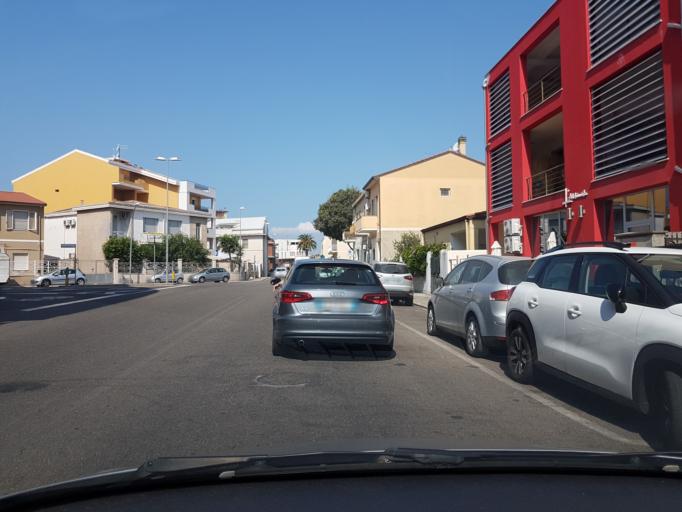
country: IT
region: Sardinia
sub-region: Provincia di Oristano
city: Oristano
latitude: 39.9083
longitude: 8.5974
